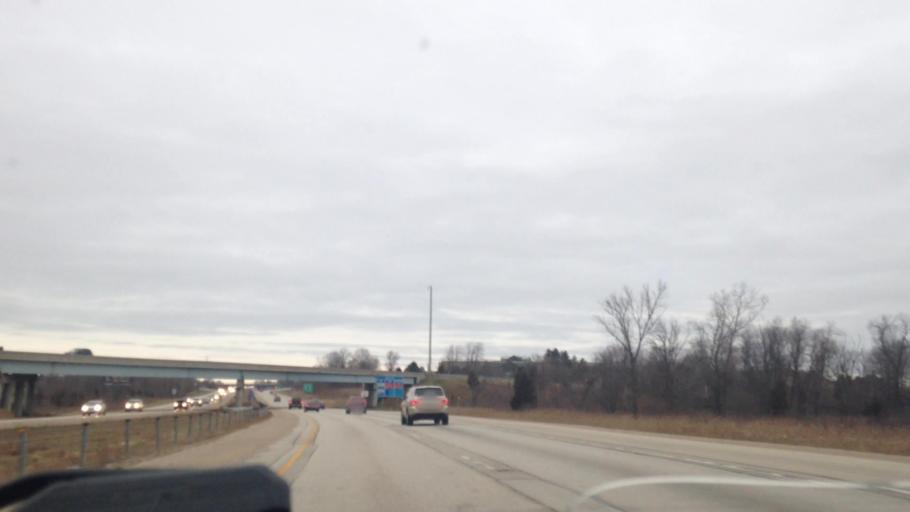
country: US
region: Wisconsin
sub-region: Washington County
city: Richfield
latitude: 43.2729
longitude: -88.1850
